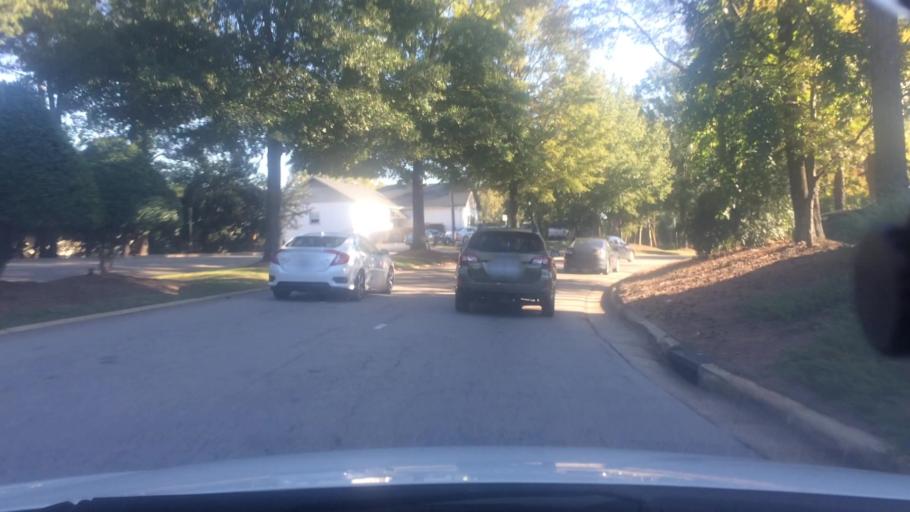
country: US
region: North Carolina
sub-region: Wake County
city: Raleigh
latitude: 35.8182
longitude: -78.6009
